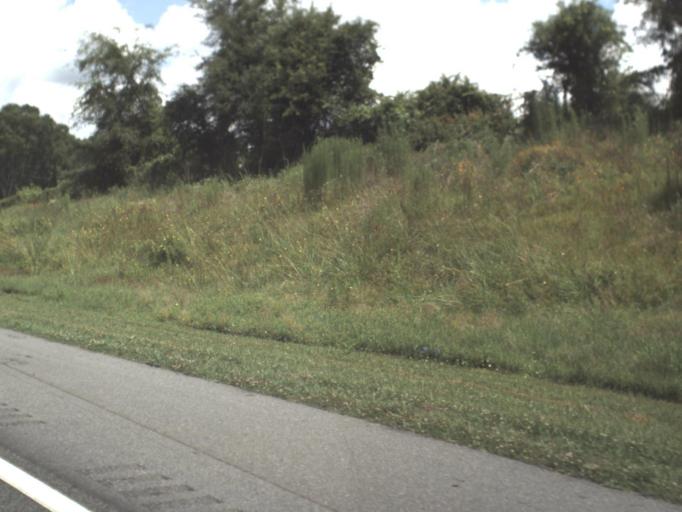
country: US
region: Florida
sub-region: Suwannee County
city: Wellborn
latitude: 30.3039
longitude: -82.7921
